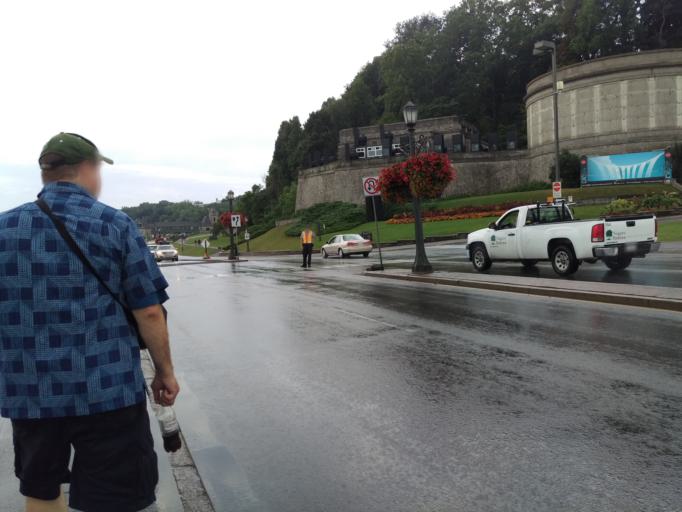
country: CA
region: Ontario
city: Niagara Falls
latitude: 43.0830
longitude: -79.0775
